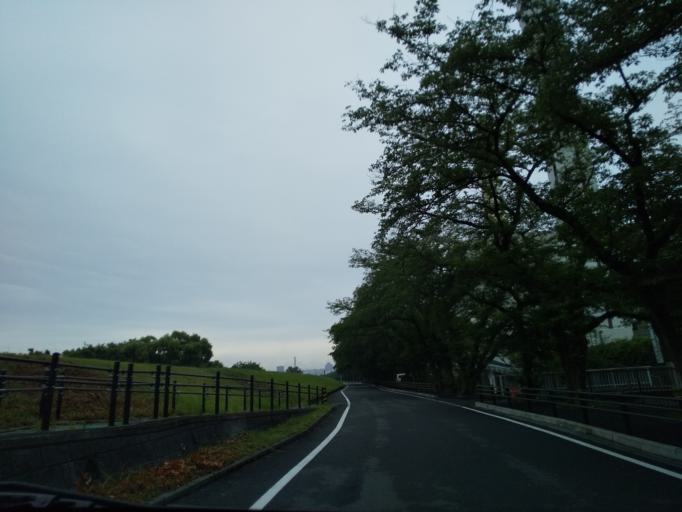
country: JP
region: Tokyo
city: Hino
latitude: 35.6674
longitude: 139.4288
